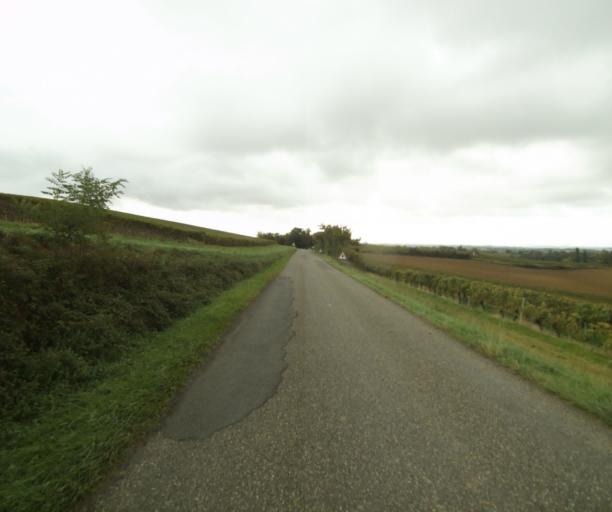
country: FR
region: Midi-Pyrenees
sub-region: Departement du Gers
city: Nogaro
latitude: 43.8283
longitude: -0.0387
